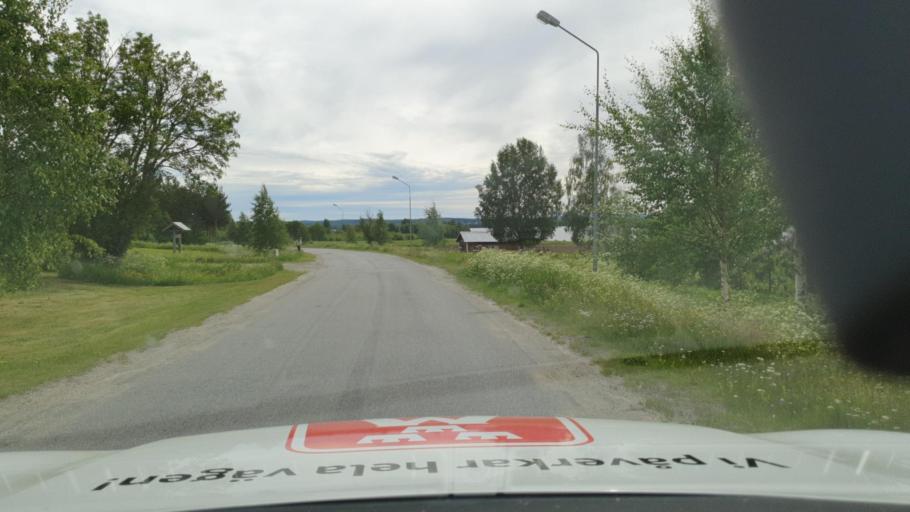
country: SE
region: Vaesterbotten
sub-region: Skelleftea Kommun
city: Burtraesk
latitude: 64.4892
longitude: 20.5053
